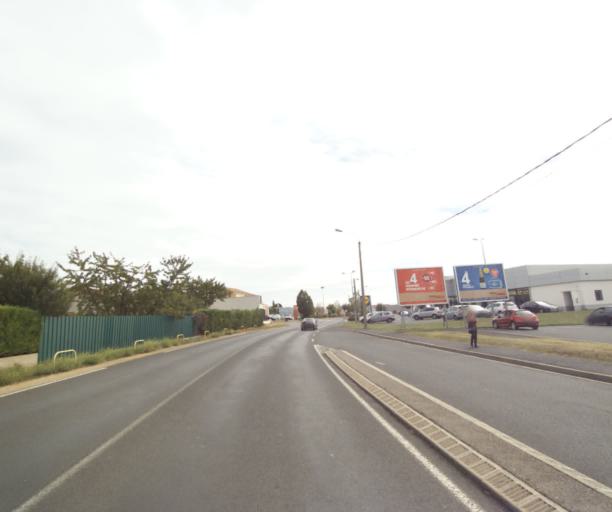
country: FR
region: Auvergne
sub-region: Departement du Puy-de-Dome
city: Le Cendre
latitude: 45.7280
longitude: 3.1879
